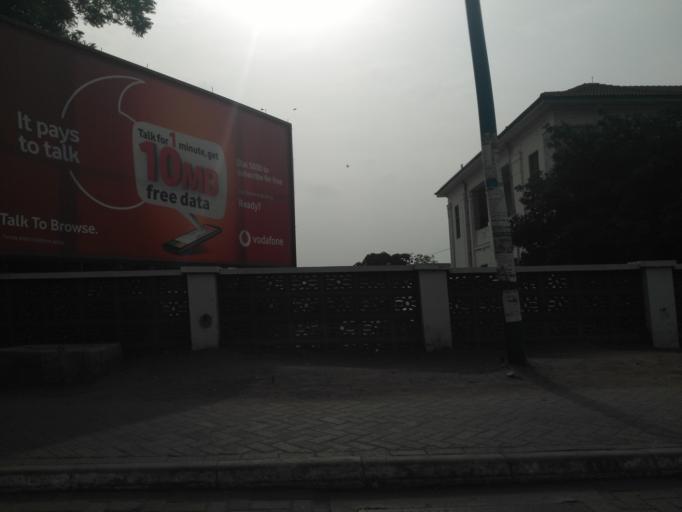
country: GH
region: Greater Accra
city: Accra
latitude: 5.5424
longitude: -0.2058
